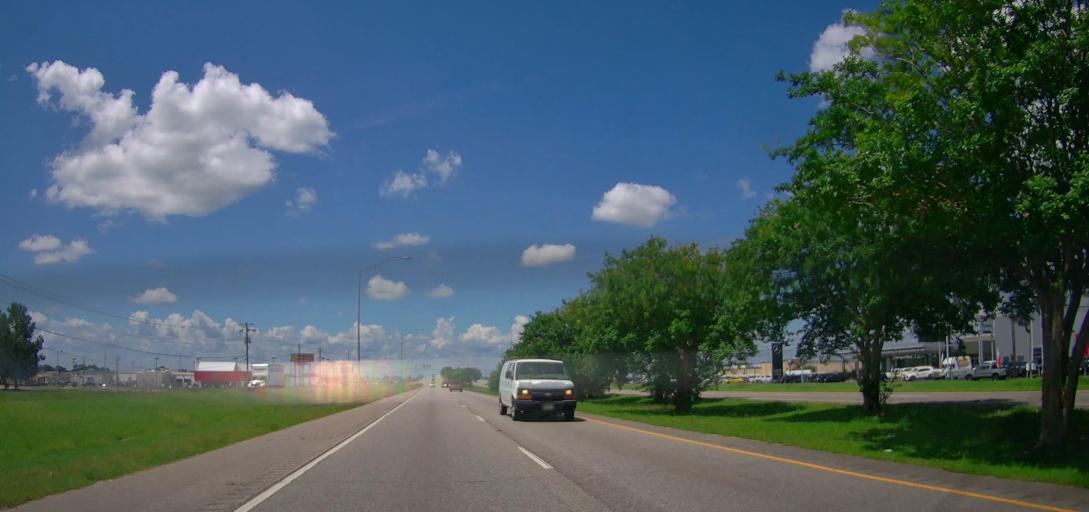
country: US
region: Alabama
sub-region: Montgomery County
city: Montgomery
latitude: 32.3766
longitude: -86.2096
